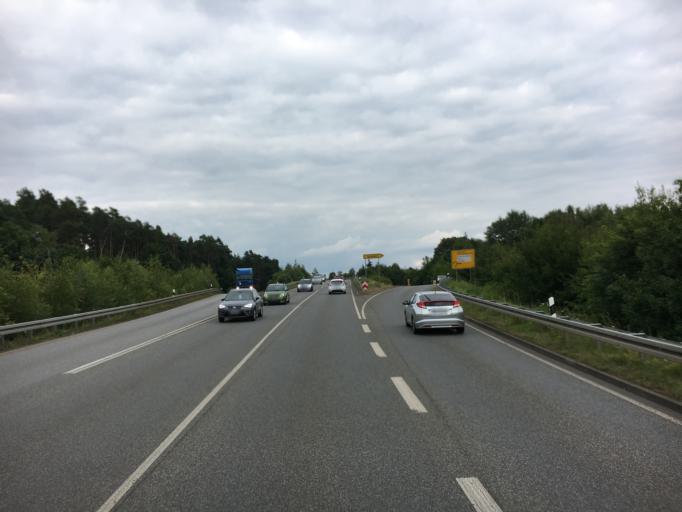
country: DE
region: Hesse
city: Stadtallendorf
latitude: 50.8276
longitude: 8.9966
